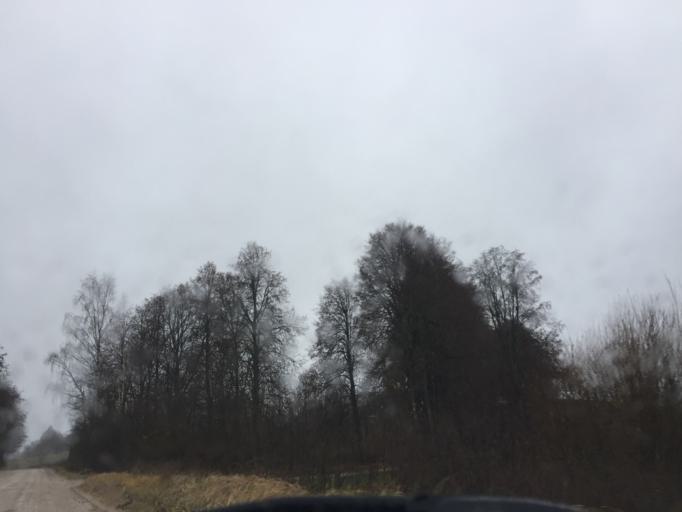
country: LV
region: Salas
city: Sala
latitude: 56.4975
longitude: 25.6854
